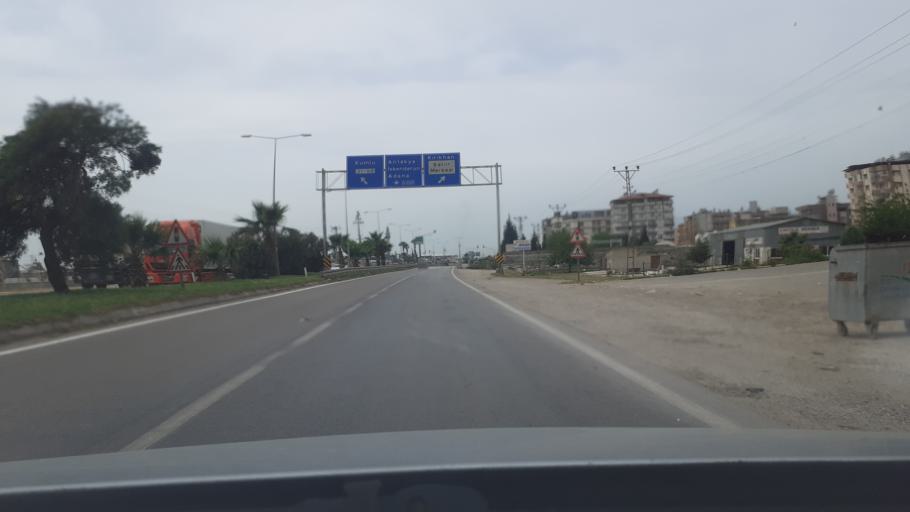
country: TR
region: Hatay
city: Kirikhan
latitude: 36.4894
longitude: 36.3682
